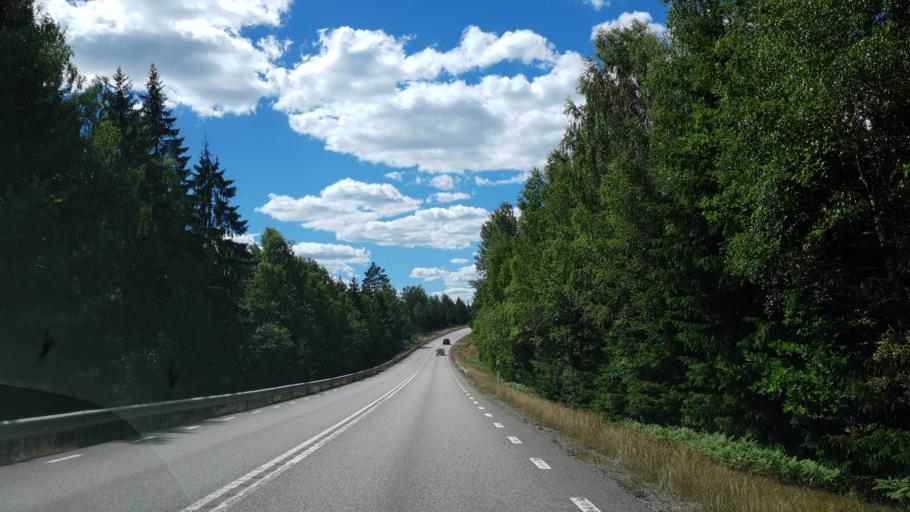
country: SE
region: Kronoberg
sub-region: Lessebo Kommun
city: Lessebo
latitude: 56.7811
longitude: 15.2109
